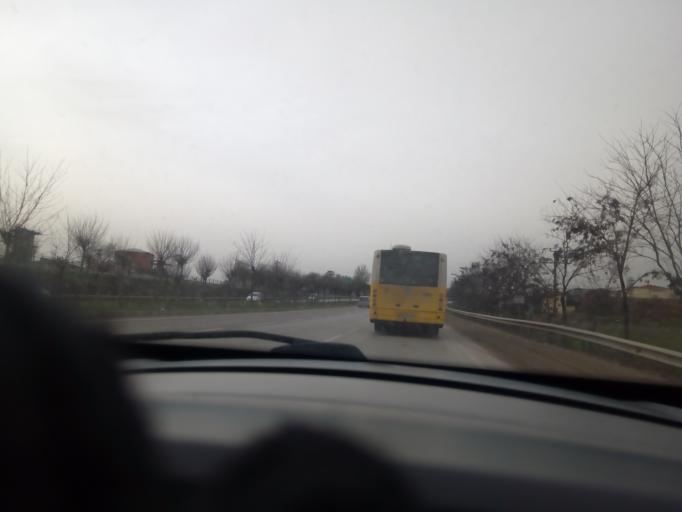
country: TR
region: Balikesir
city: Susurluk
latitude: 39.9509
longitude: 28.1700
